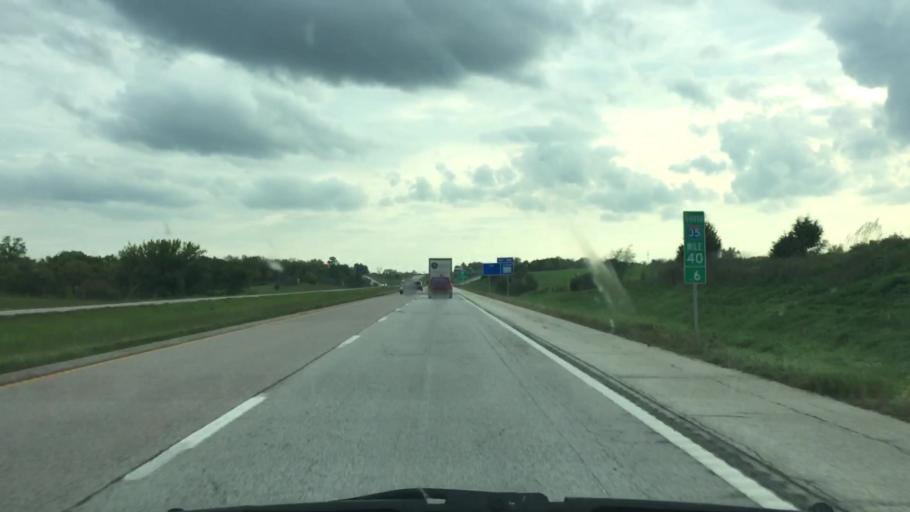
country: US
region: Missouri
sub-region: Clinton County
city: Lathrop
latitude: 39.5601
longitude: -94.2667
